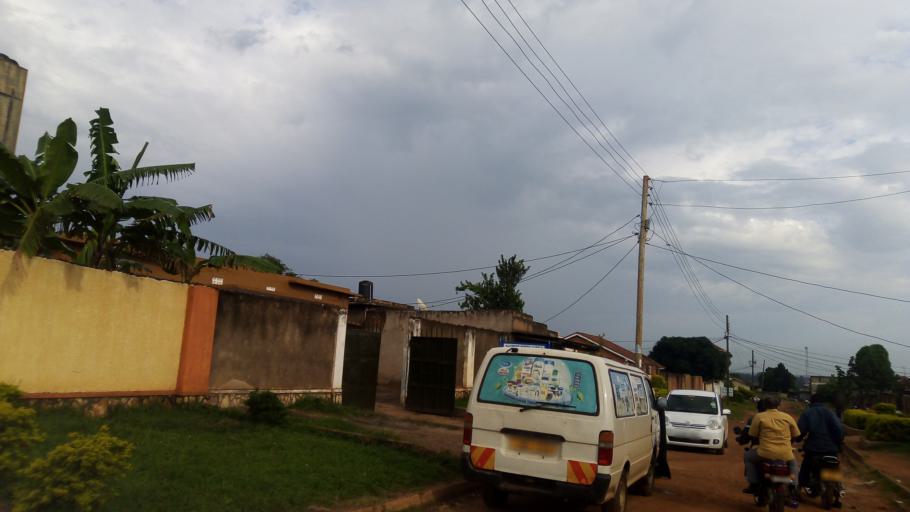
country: UG
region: Eastern Region
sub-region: Mbale District
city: Mbale
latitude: 1.0789
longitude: 34.1668
